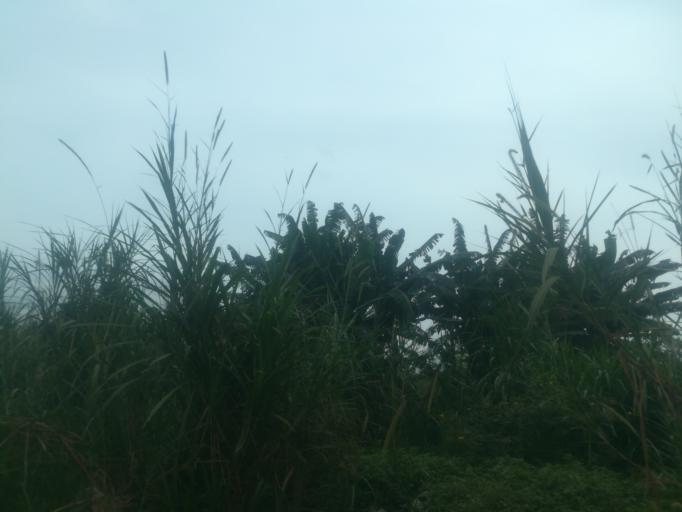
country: NG
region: Oyo
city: Ibadan
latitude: 7.3765
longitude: 3.9560
